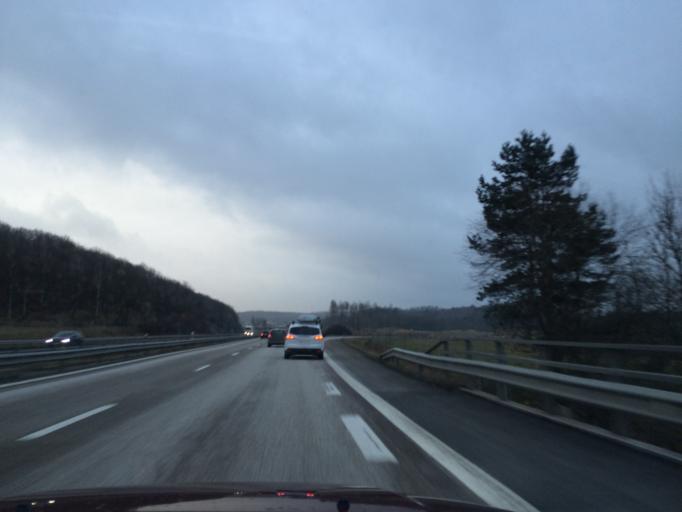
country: SE
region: Halland
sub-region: Kungsbacka Kommun
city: Kungsbacka
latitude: 57.5169
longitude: 12.0507
